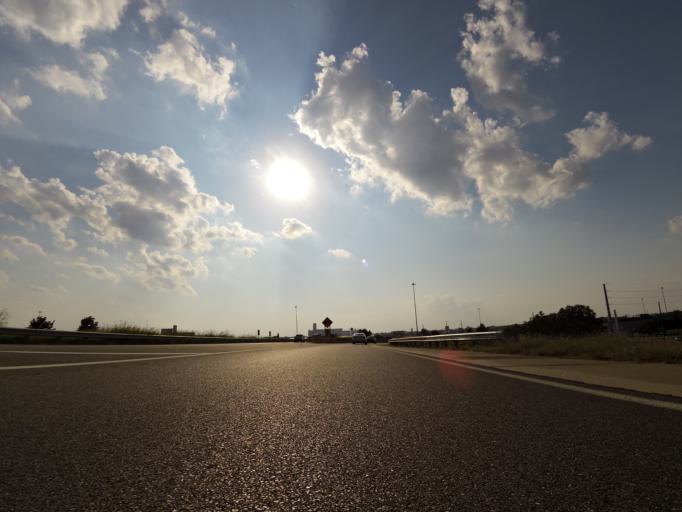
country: US
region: Kansas
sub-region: Sedgwick County
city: Bellaire
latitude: 37.7437
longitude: -97.3159
